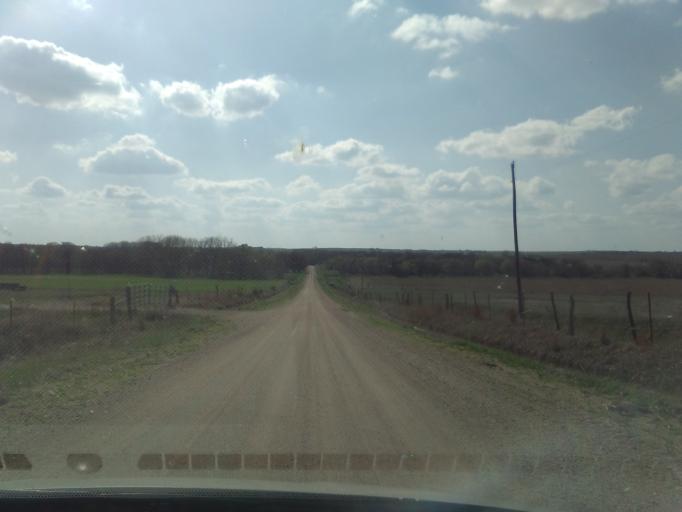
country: US
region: Nebraska
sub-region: Webster County
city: Red Cloud
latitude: 40.0313
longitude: -98.4516
